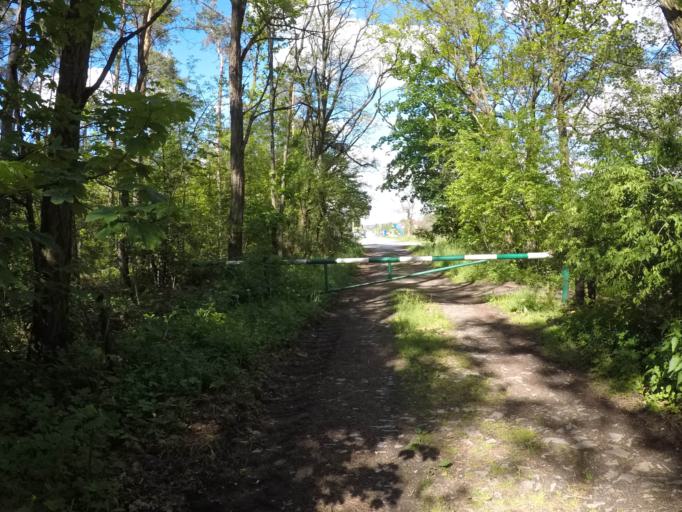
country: PL
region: Swietokrzyskie
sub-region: Powiat kielecki
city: Kostomloty Drugie
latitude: 50.8957
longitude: 20.5475
